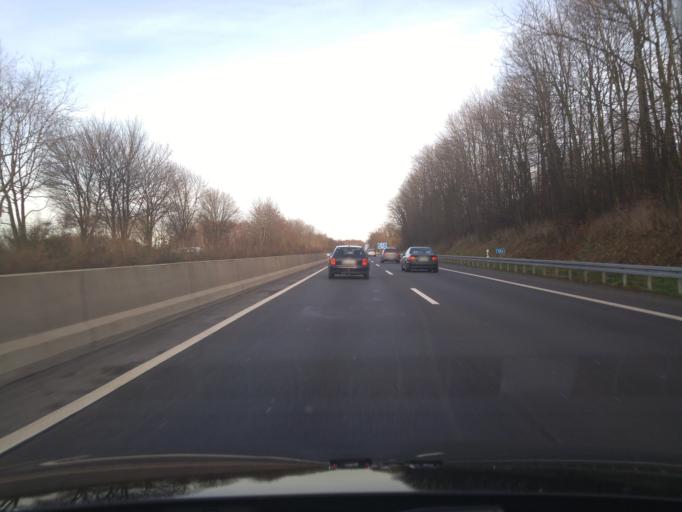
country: DE
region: North Rhine-Westphalia
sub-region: Regierungsbezirk Dusseldorf
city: Muelheim (Ruhr)
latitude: 51.3911
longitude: 6.9379
